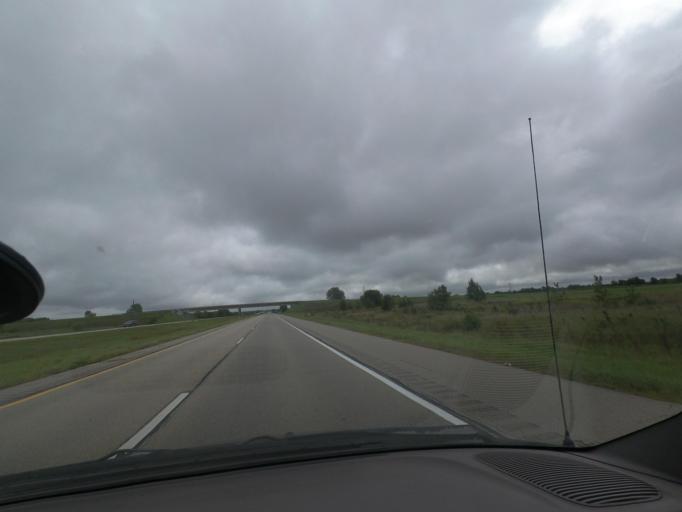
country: US
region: Illinois
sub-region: Piatt County
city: Monticello
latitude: 40.0307
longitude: -88.6342
